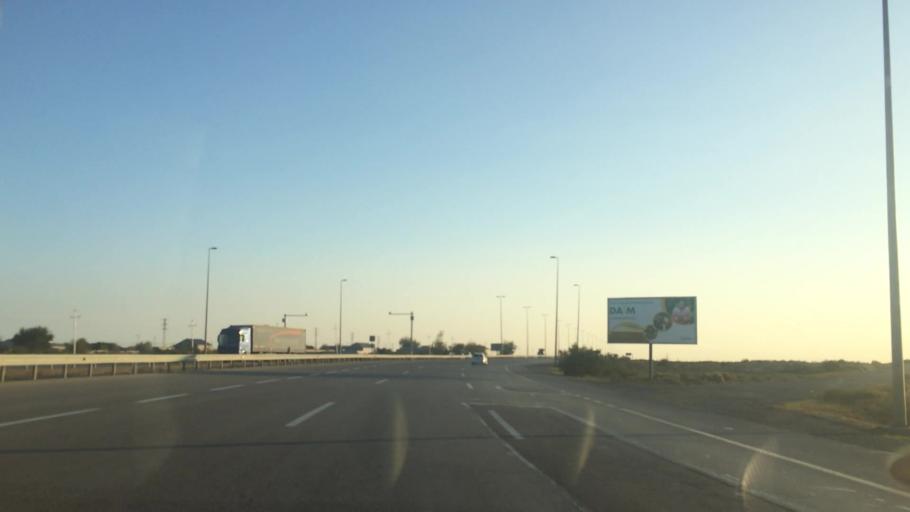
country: AZ
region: Baki
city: Qobustan
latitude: 39.9915
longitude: 49.4301
